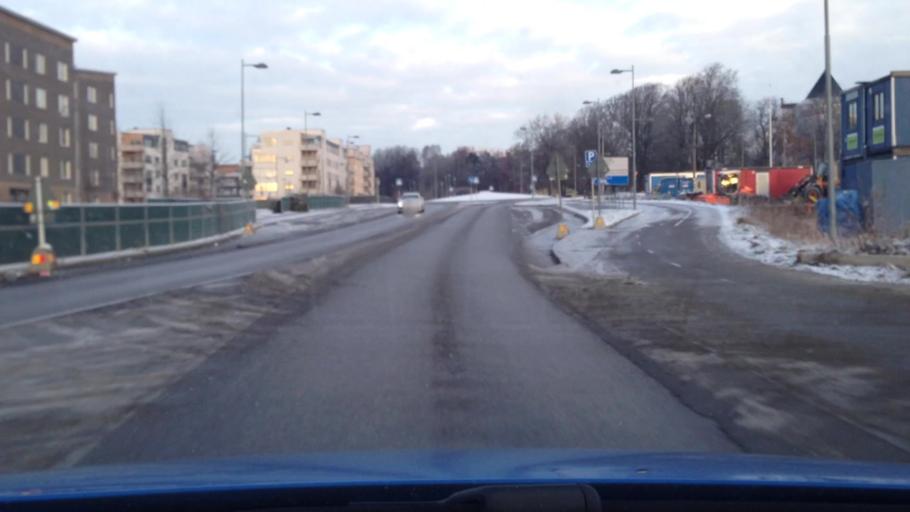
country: SE
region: Vaestra Goetaland
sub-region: Goteborg
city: Eriksbo
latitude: 57.7327
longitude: 12.0305
